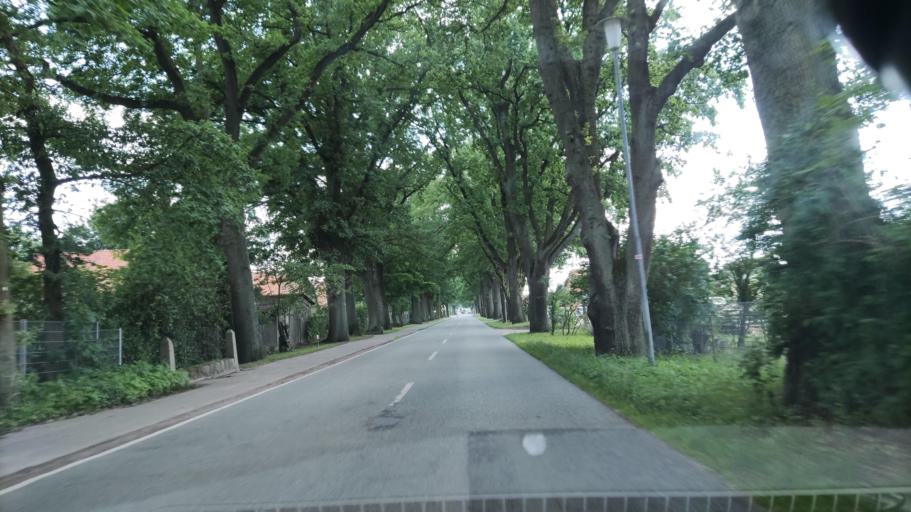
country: DE
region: Mecklenburg-Vorpommern
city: Lubtheen
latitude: 53.3417
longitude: 11.1428
